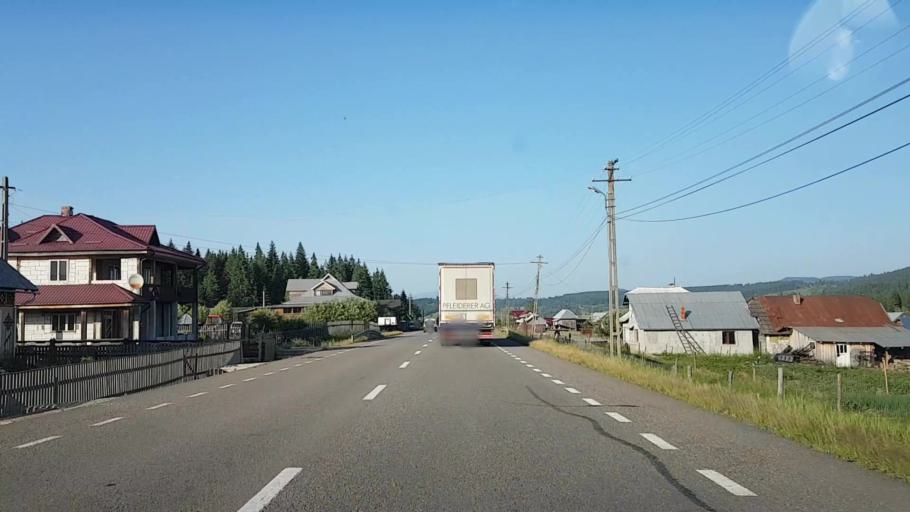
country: RO
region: Suceava
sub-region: Comuna Poiana Stampei
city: Poiana Stampei
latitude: 47.3049
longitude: 25.1178
